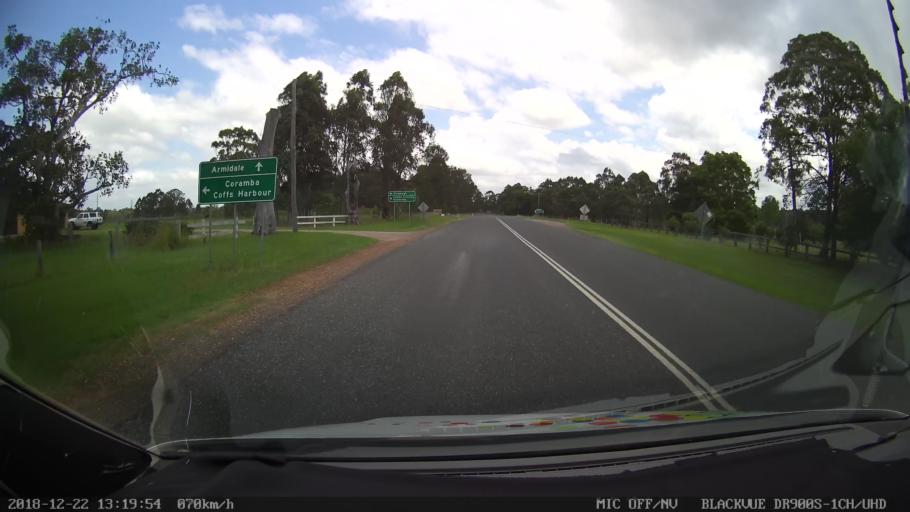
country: AU
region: New South Wales
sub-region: Clarence Valley
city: South Grafton
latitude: -29.7608
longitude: 152.9305
